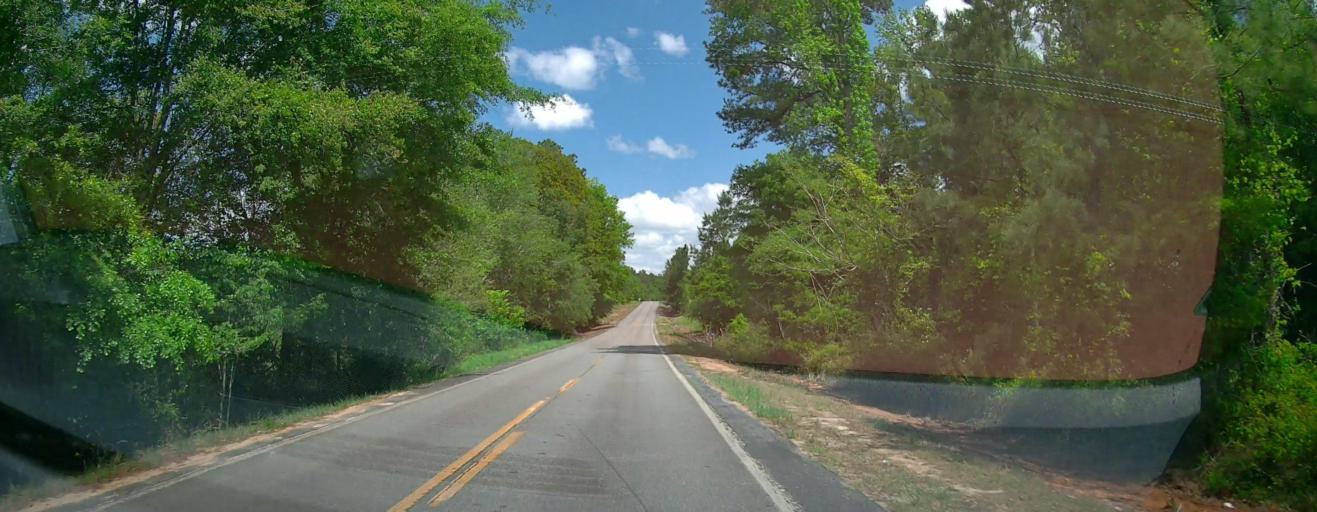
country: US
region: Georgia
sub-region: Bleckley County
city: Cochran
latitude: 32.4539
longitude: -83.2867
